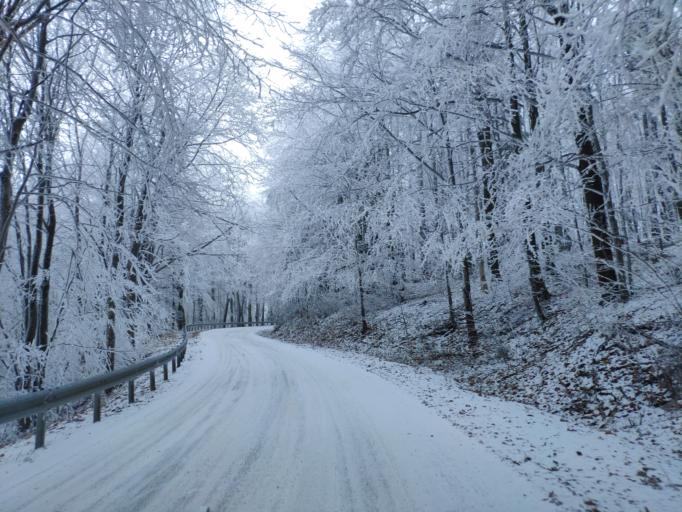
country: SK
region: Kosicky
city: Dobsina
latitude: 48.8101
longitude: 20.4819
